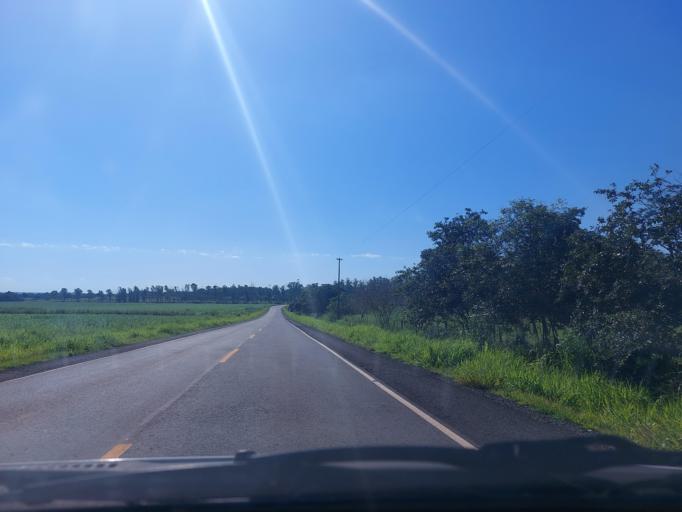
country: PY
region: San Pedro
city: Guayaybi
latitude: -24.3203
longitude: -56.1842
